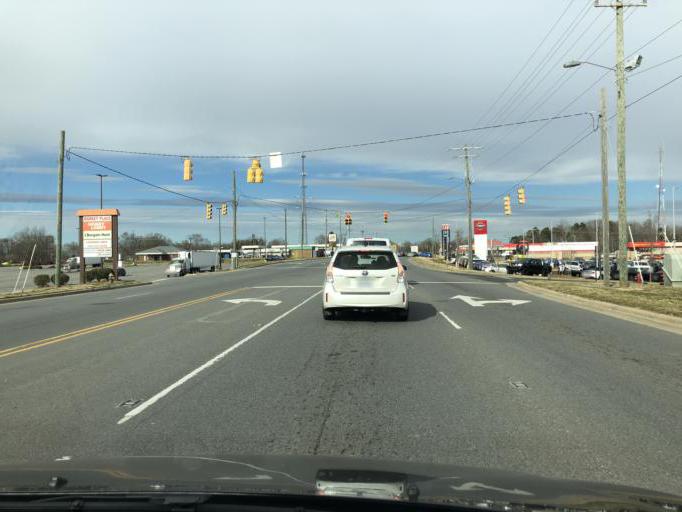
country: US
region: North Carolina
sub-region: Cleveland County
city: Shelby
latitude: 35.2698
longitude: -81.4975
